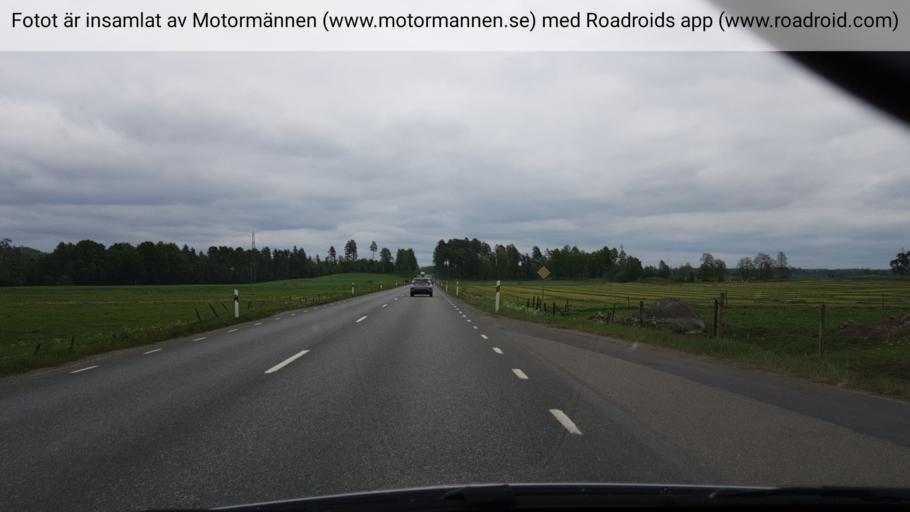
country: SE
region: Joenkoeping
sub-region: Vetlanda Kommun
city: Landsbro
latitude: 57.4005
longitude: 14.9134
